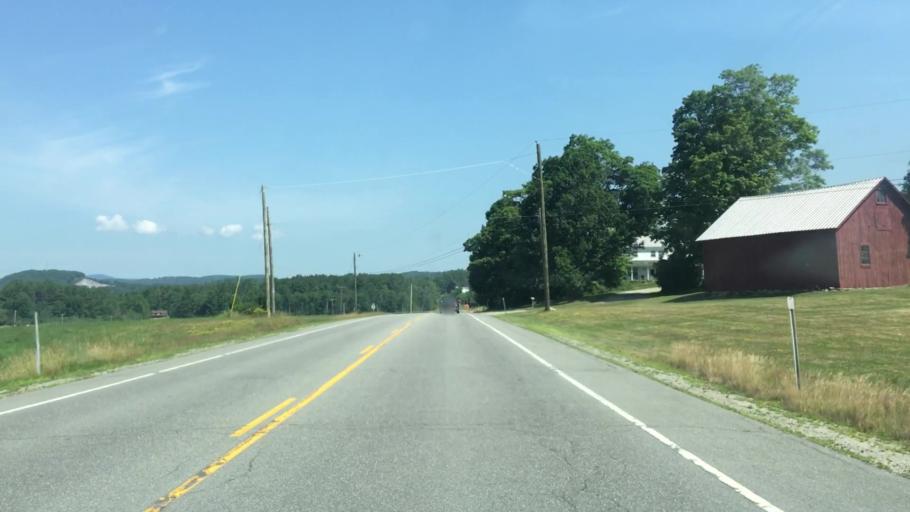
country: US
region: New Hampshire
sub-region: Sullivan County
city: Sunapee
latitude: 43.3618
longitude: -72.1200
